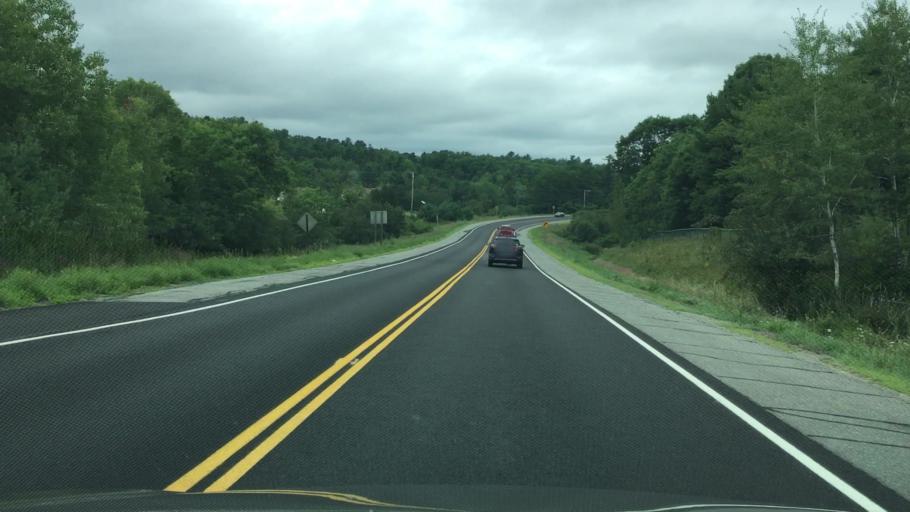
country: US
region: Maine
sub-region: Penobscot County
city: Orrington
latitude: 44.6962
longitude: -68.8167
